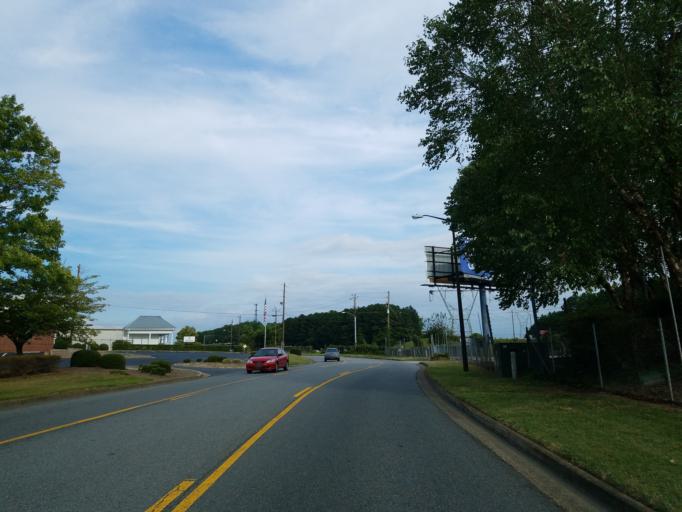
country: US
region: Georgia
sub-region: Cobb County
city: Marietta
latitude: 33.9976
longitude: -84.5326
